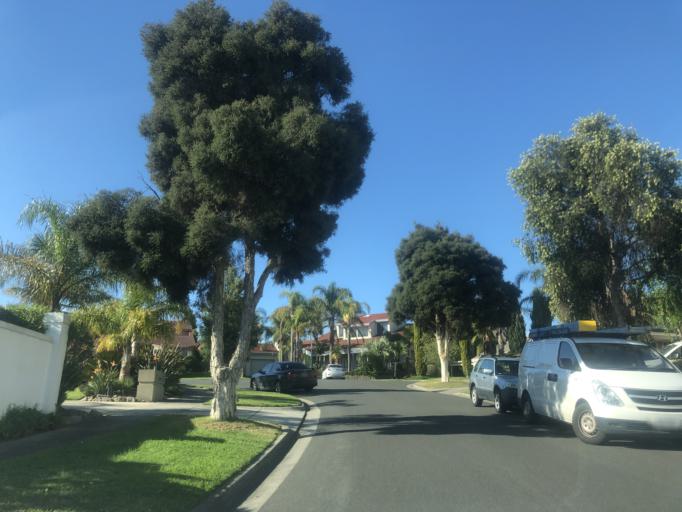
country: AU
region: Victoria
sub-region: Monash
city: Mulgrave
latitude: -37.9194
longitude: 145.1947
